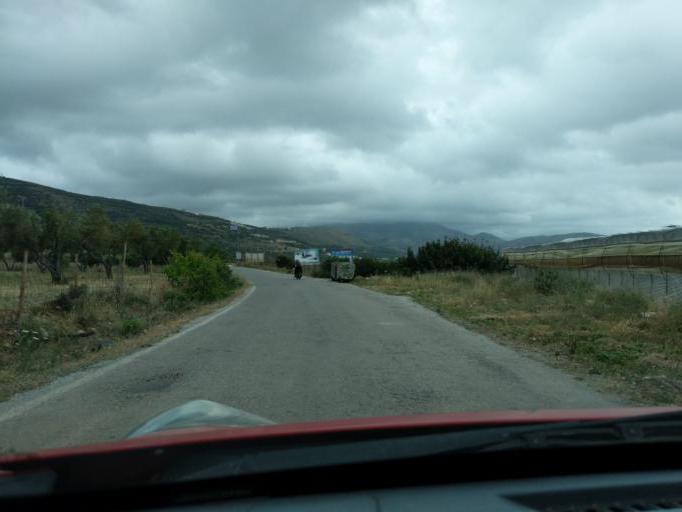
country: GR
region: Crete
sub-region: Nomos Chanias
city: Platanos
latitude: 35.4946
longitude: 23.5854
